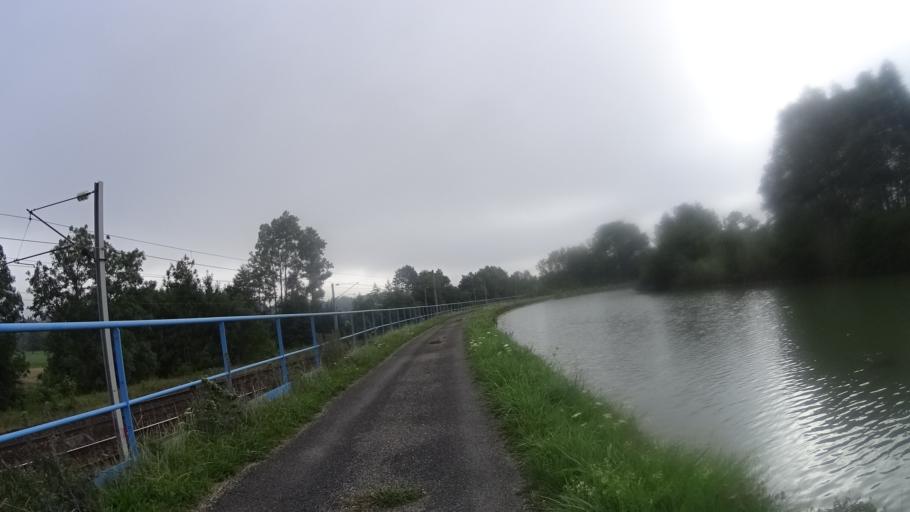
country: FR
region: Lorraine
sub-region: Departement de la Meuse
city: Fains-Veel
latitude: 48.8070
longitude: 5.0825
